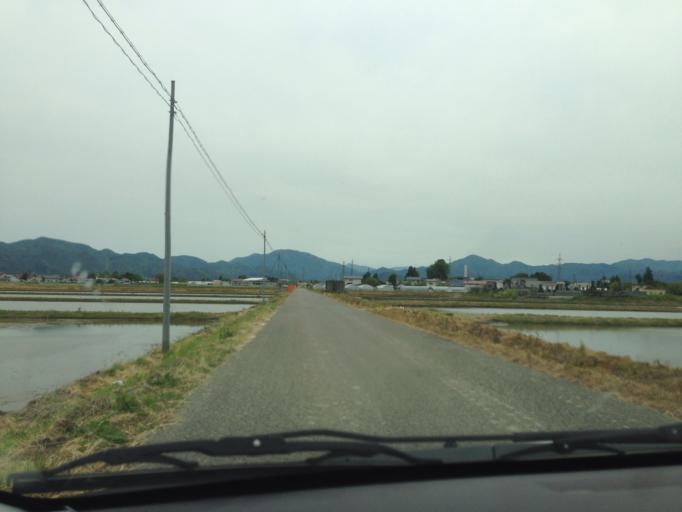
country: JP
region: Fukushima
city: Kitakata
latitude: 37.5087
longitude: 139.8943
